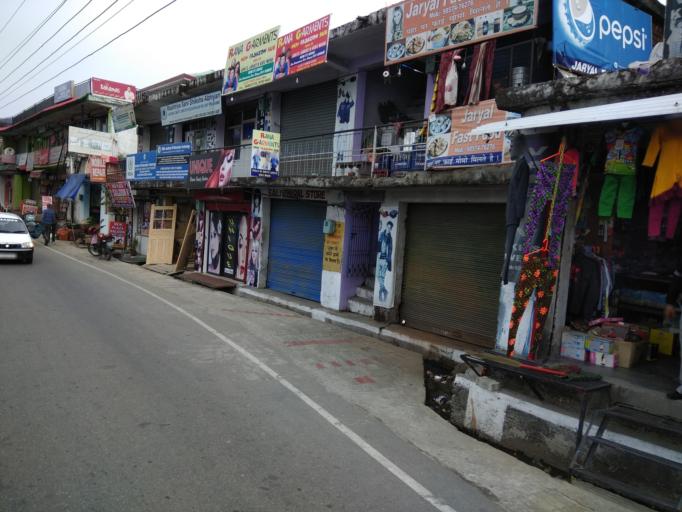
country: IN
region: Himachal Pradesh
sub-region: Kangra
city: Dharmsala
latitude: 32.2003
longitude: 76.3357
